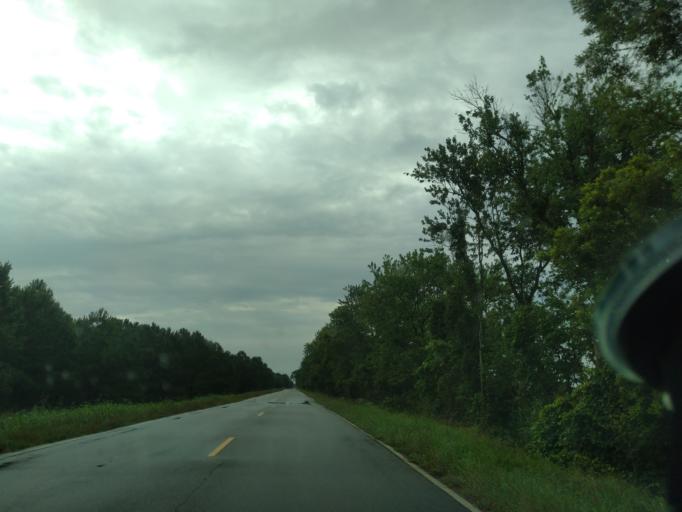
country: US
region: North Carolina
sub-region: Washington County
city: Plymouth
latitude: 35.8428
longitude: -76.5503
